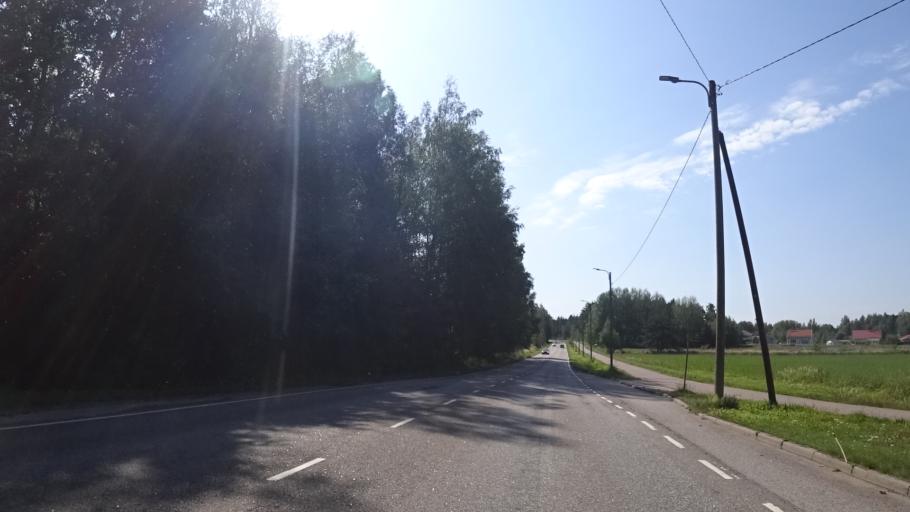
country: FI
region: Kymenlaakso
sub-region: Kotka-Hamina
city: Karhula
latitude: 60.5081
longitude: 26.9647
